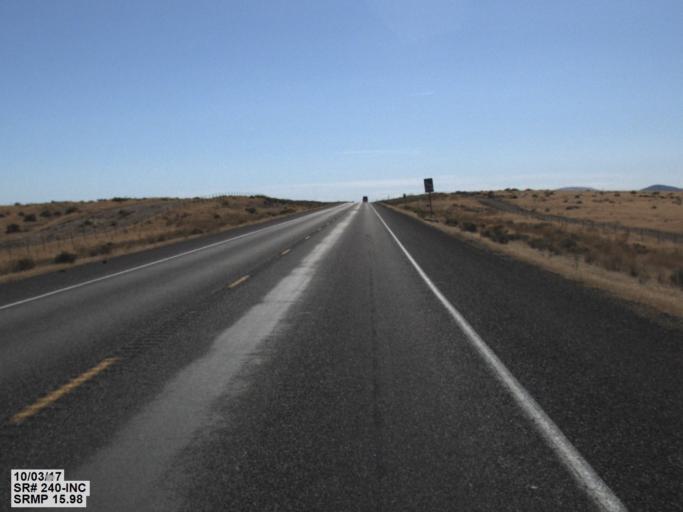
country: US
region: Washington
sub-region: Benton County
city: Benton City
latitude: 46.4337
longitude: -119.4814
